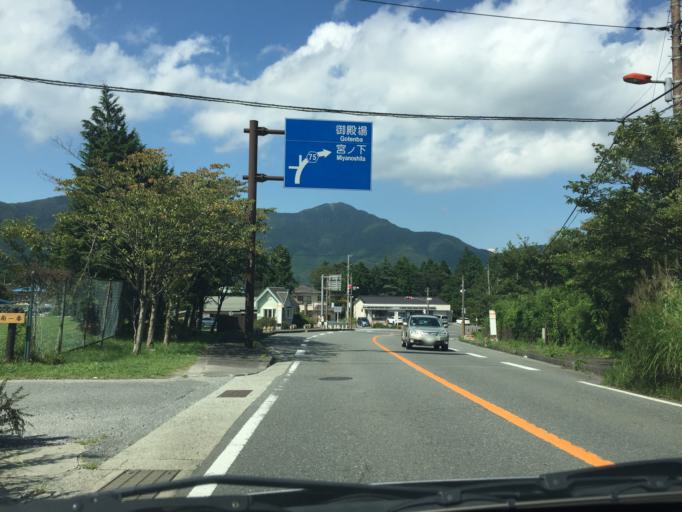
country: JP
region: Shizuoka
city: Gotemba
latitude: 35.2584
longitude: 139.0008
